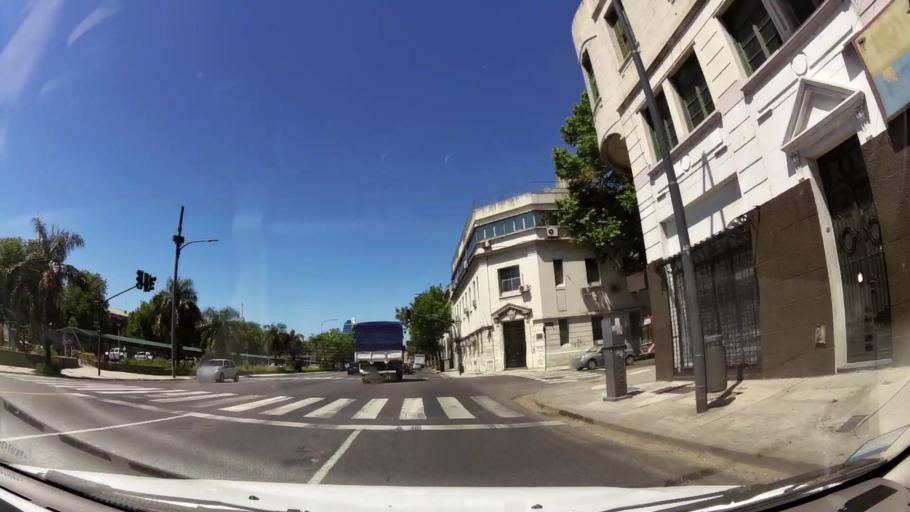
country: AR
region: Buenos Aires F.D.
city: Buenos Aires
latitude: -34.6190
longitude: -58.3663
